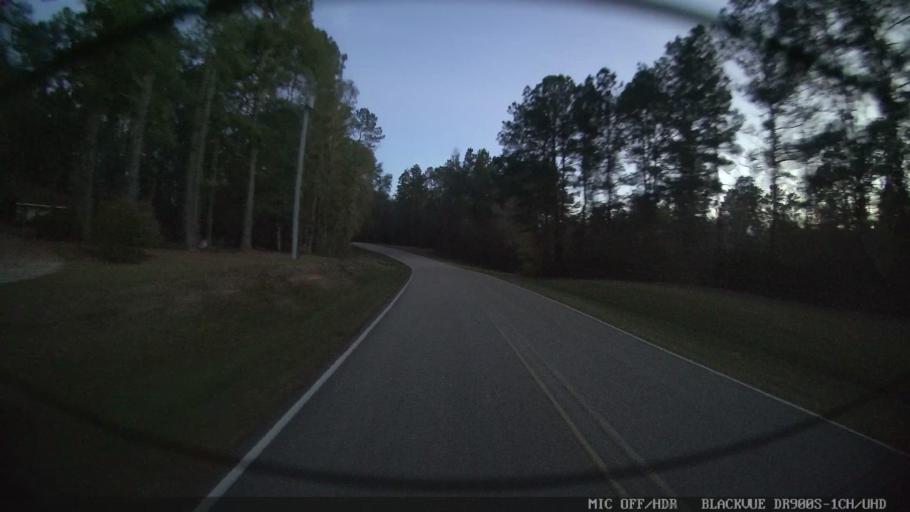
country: US
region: Mississippi
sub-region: Perry County
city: New Augusta
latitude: 31.1569
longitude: -89.2107
